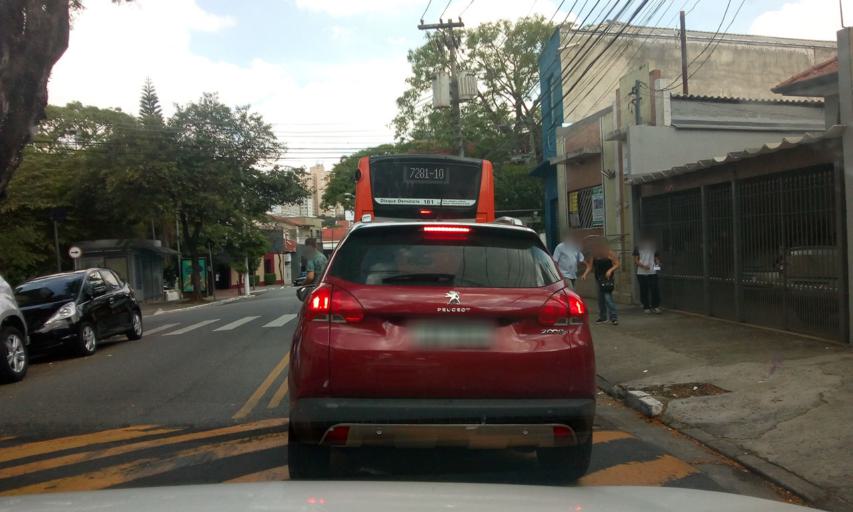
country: BR
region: Sao Paulo
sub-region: Sao Paulo
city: Sao Paulo
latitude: -23.5332
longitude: -46.7044
